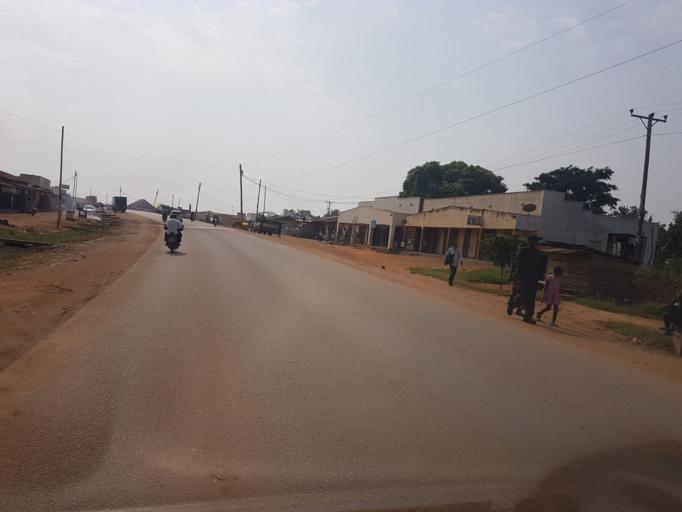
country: UG
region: Western Region
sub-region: Mbarara District
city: Mbarara
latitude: -0.6346
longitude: 30.6186
